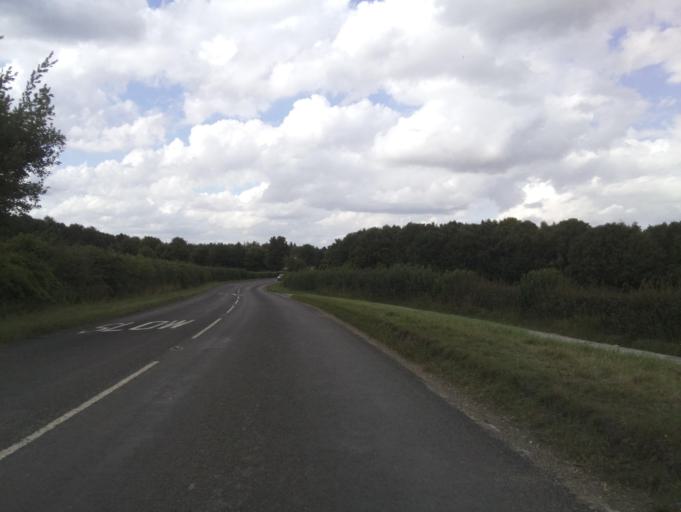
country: GB
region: England
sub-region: North Yorkshire
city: Ripon
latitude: 54.1799
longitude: -1.5585
